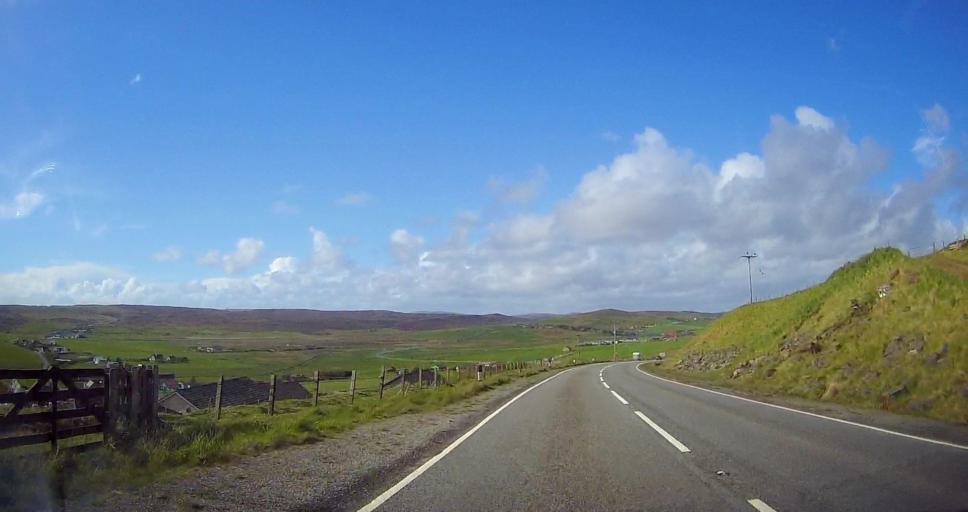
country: GB
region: Scotland
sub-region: Shetland Islands
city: Lerwick
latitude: 60.1801
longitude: -1.2246
